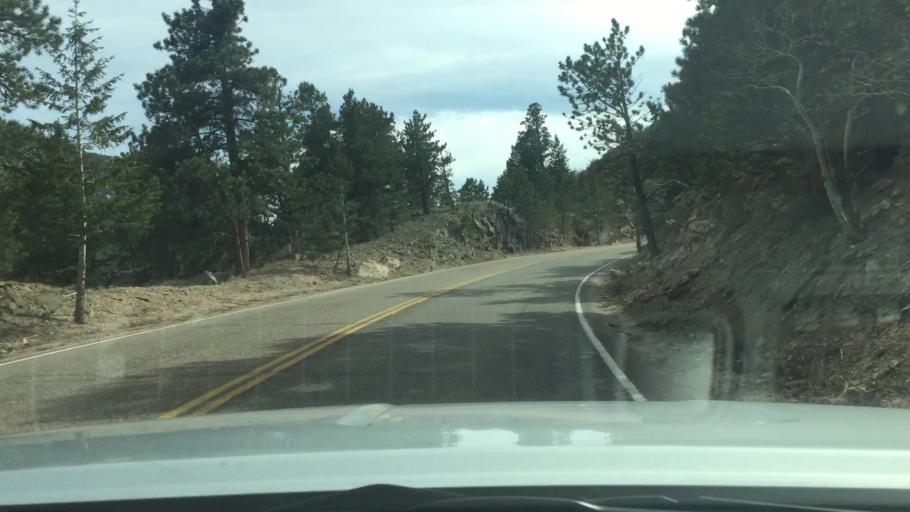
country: US
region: Colorado
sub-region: Larimer County
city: Estes Park
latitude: 40.3264
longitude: -105.5299
